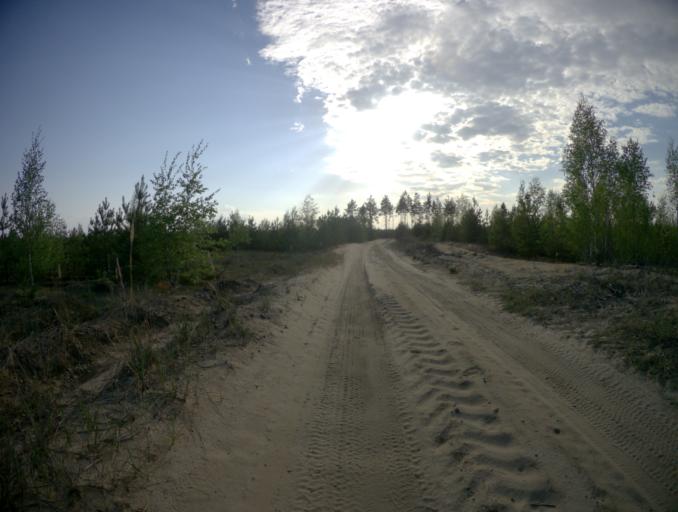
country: RU
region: Vladimir
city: Vyazniki
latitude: 56.4057
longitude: 42.1887
